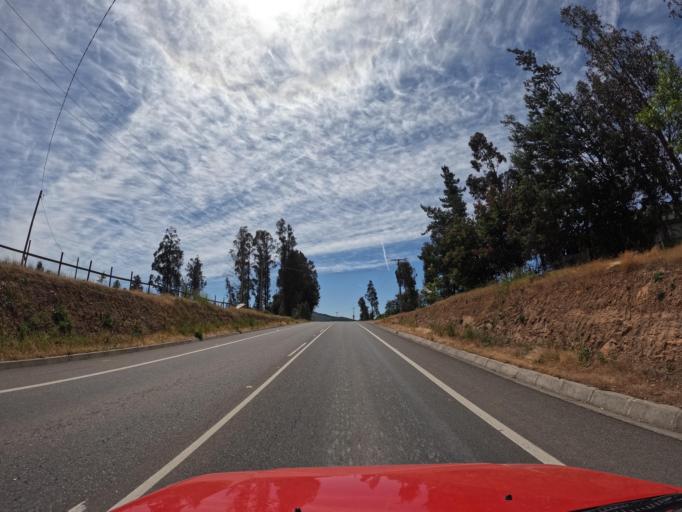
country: CL
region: Maule
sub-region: Provincia de Talca
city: Talca
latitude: -35.2838
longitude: -71.5308
